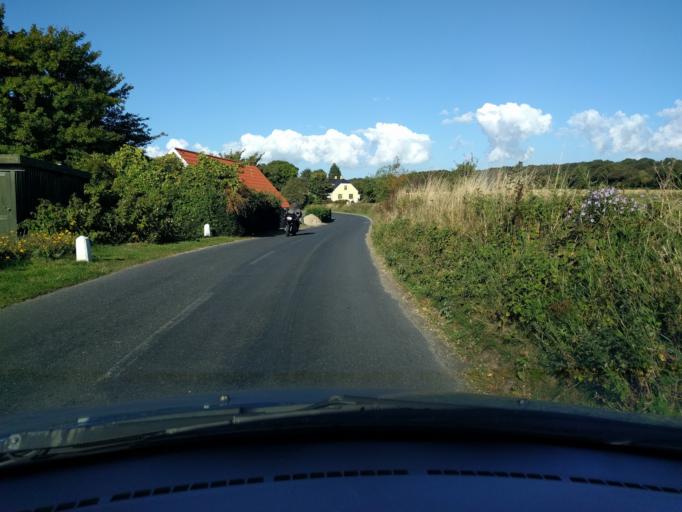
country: DK
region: South Denmark
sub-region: Assens Kommune
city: Harby
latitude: 55.1417
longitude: 10.0199
